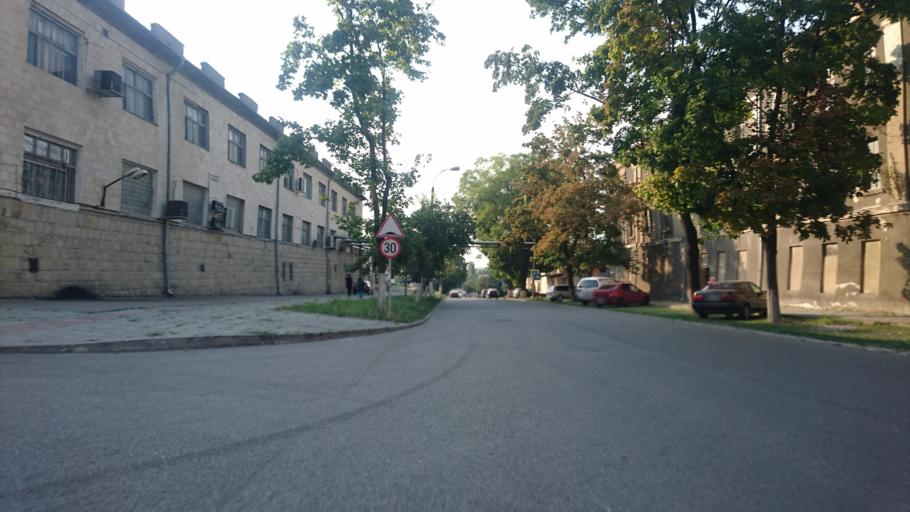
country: MD
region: Chisinau
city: Chisinau
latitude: 47.0344
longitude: 28.8244
